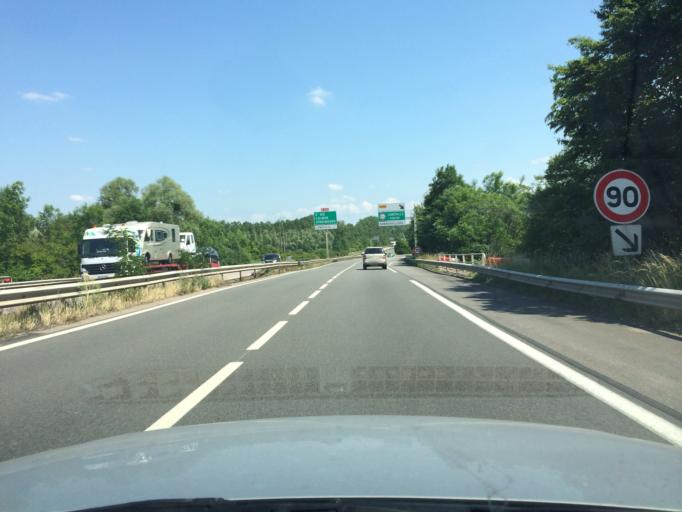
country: FR
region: Lorraine
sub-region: Departement de Meurthe-et-Moselle
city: Luneville
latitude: 48.5758
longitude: 6.4814
